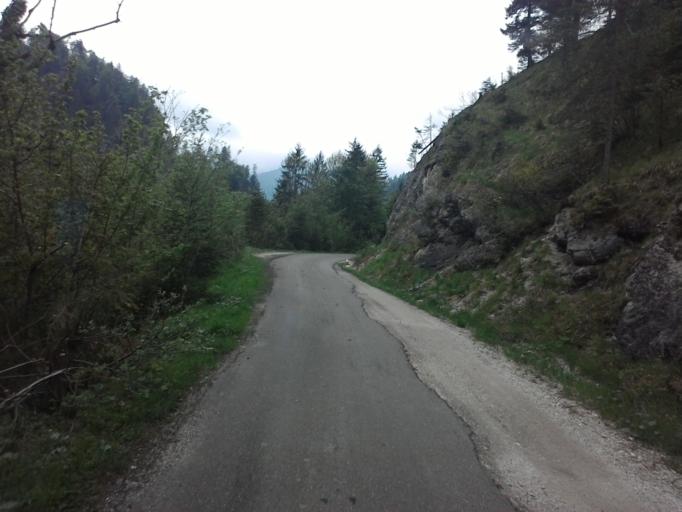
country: AT
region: Styria
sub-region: Politischer Bezirk Liezen
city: Wildalpen
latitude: 47.7019
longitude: 14.9614
